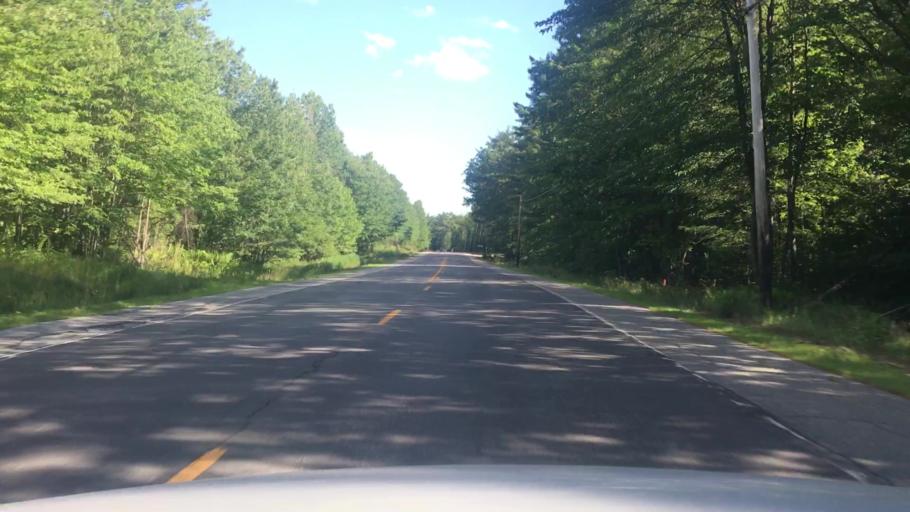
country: US
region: Maine
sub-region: Franklin County
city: Jay
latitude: 44.5319
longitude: -70.2325
